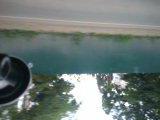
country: RU
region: Moskovskaya
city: Bykovo
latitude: 55.6172
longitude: 38.0976
